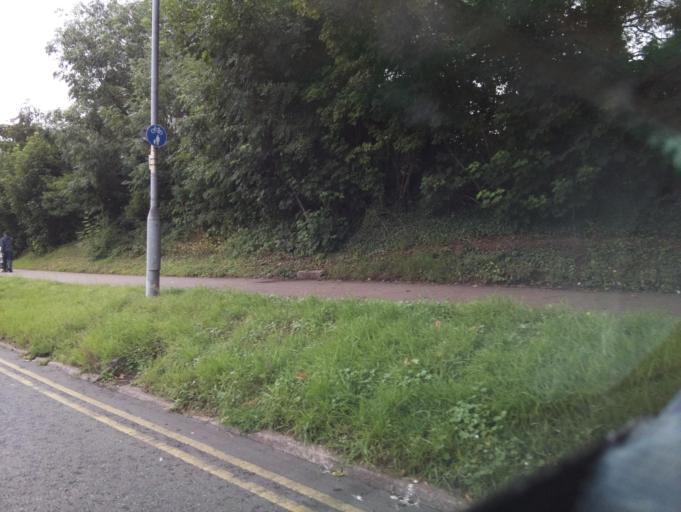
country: GB
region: England
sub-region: Lincolnshire
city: Stamford
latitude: 52.6589
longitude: -0.4660
